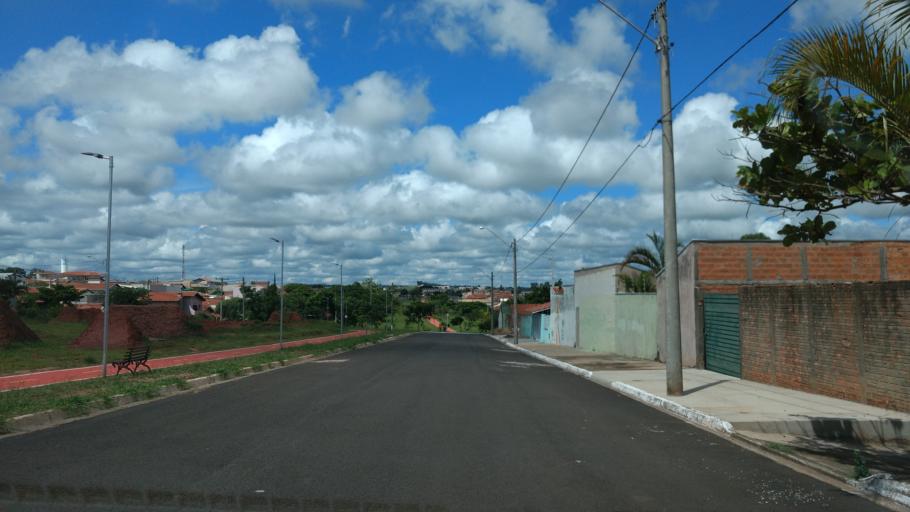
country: BR
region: Sao Paulo
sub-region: Botucatu
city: Botucatu
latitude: -22.8542
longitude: -48.4423
